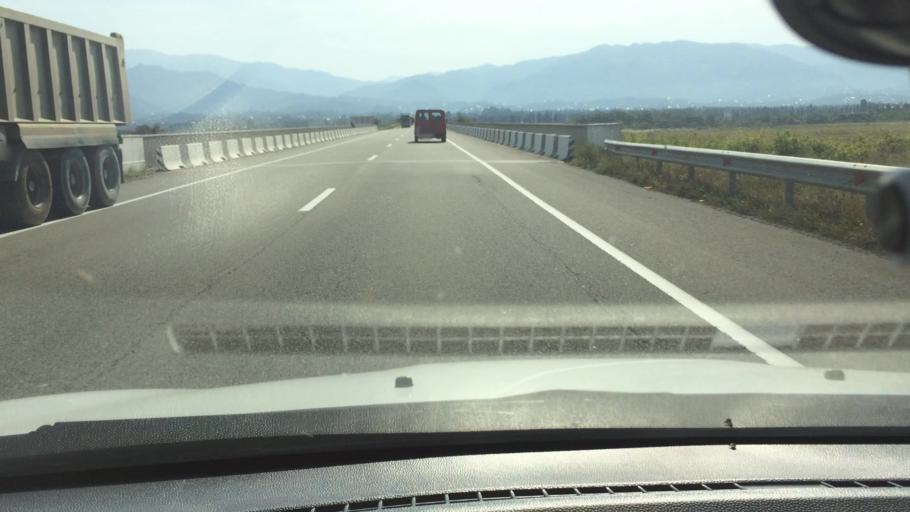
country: GE
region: Ajaria
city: Ochkhamuri
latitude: 41.8722
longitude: 41.8294
